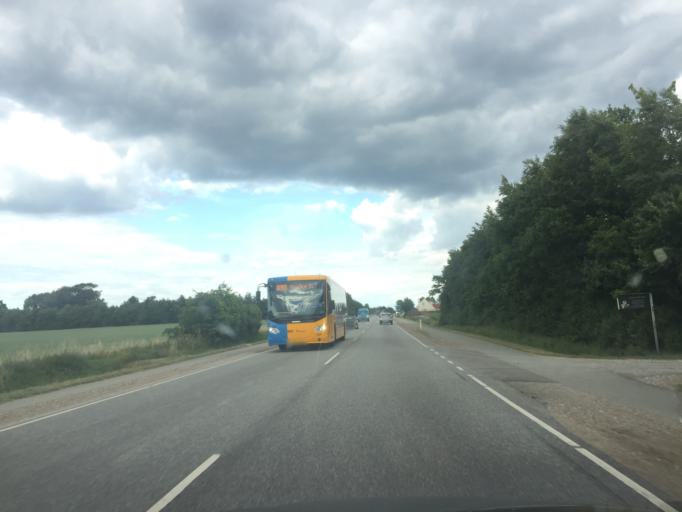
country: DK
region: Capital Region
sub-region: Frederikssund Kommune
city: Slangerup
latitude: 55.8963
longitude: 12.2179
